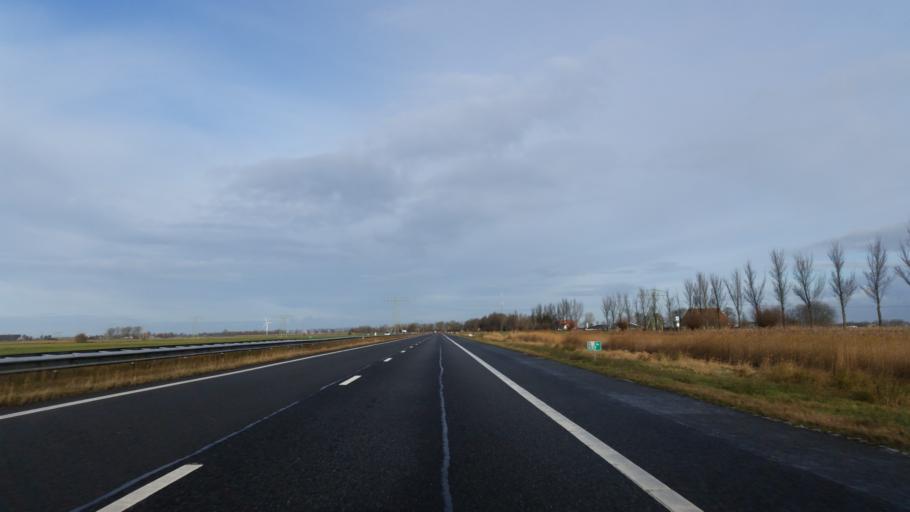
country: NL
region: Friesland
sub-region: Gemeente Boarnsterhim
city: Nes
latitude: 53.0123
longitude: 5.8700
